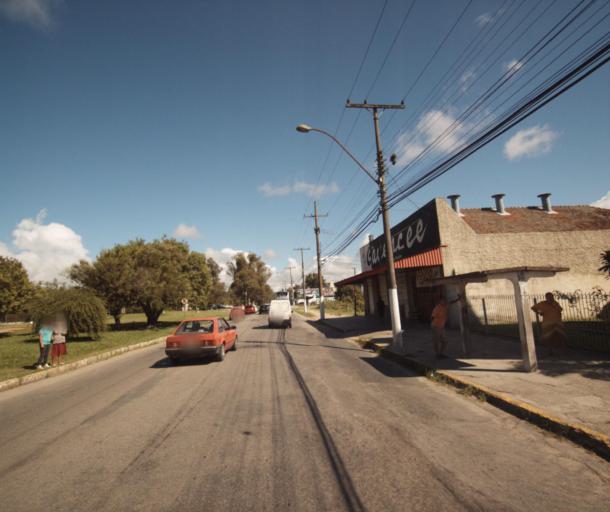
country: BR
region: Rio Grande do Sul
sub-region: Pelotas
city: Pelotas
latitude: -31.7638
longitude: -52.3555
